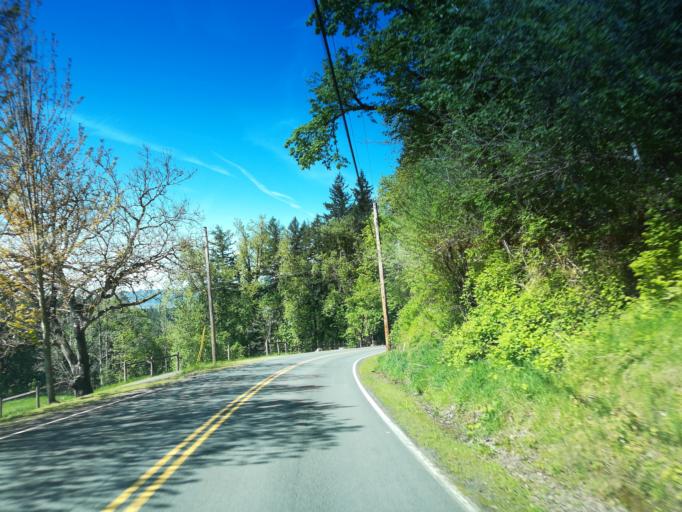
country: US
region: Oregon
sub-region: Multnomah County
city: Troutdale
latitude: 45.5258
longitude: -122.3681
